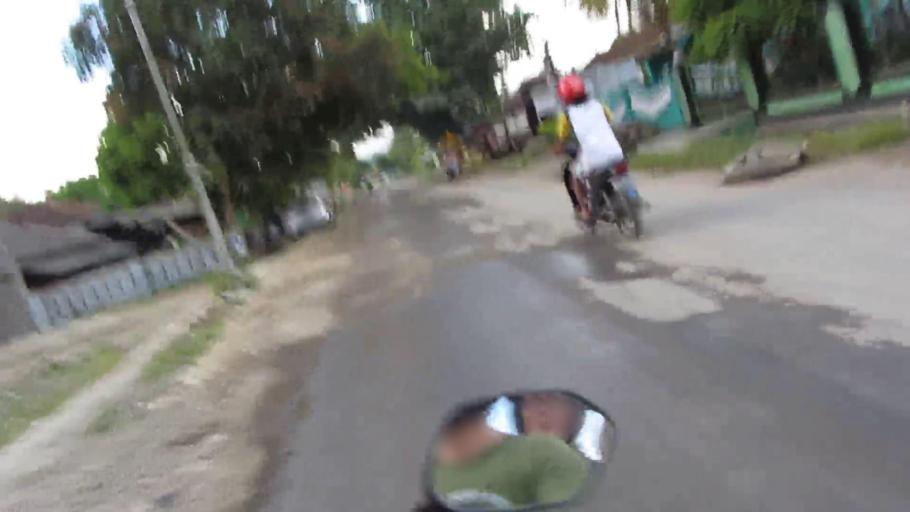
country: ID
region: West Java
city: Binangun
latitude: -7.7207
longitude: 108.4742
